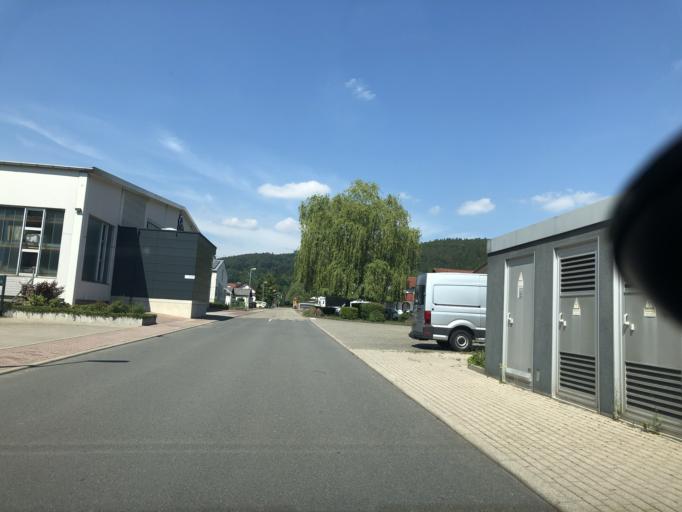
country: DE
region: Baden-Wuerttemberg
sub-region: Karlsruhe Region
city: Schonau
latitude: 49.4235
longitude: 8.8073
